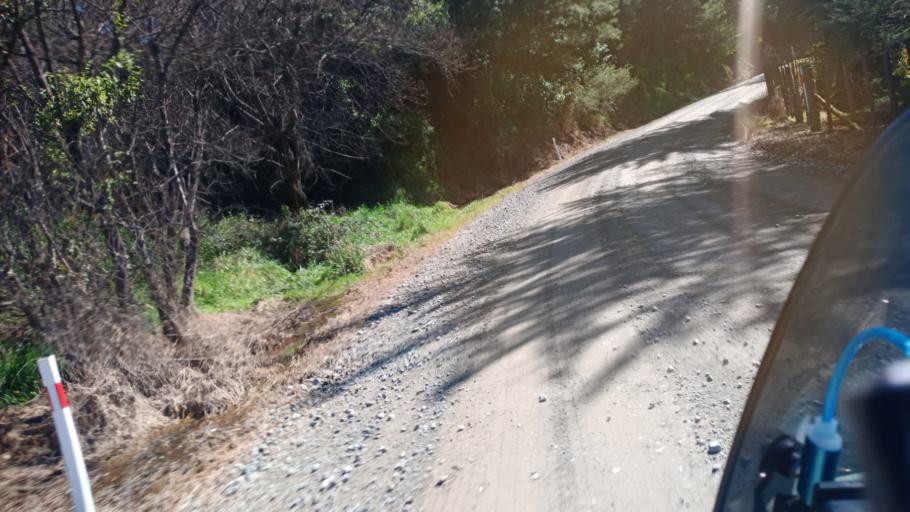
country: NZ
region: Gisborne
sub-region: Gisborne District
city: Gisborne
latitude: -37.9902
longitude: 178.2894
